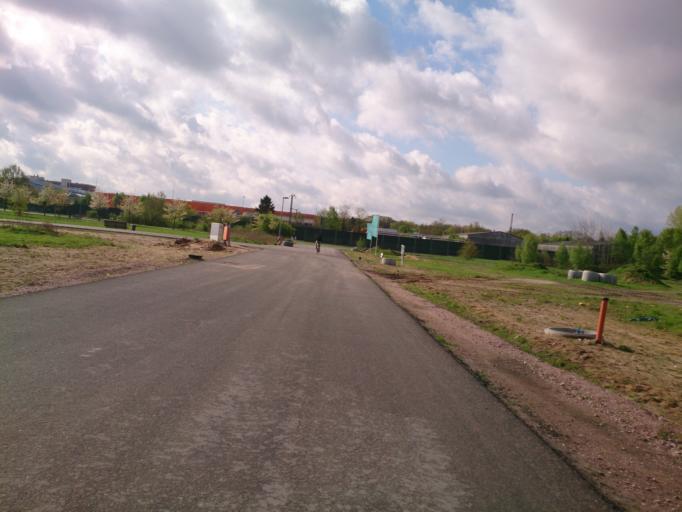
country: DE
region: Lower Saxony
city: Neu Wulmstorf
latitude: 53.4762
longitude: 9.8461
